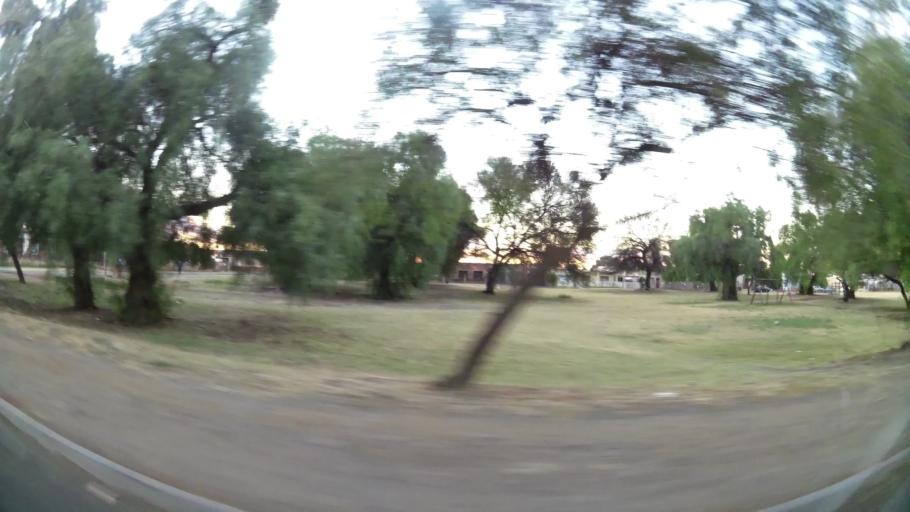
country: ZA
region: Northern Cape
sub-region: Frances Baard District Municipality
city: Kimberley
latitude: -28.7191
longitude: 24.7738
